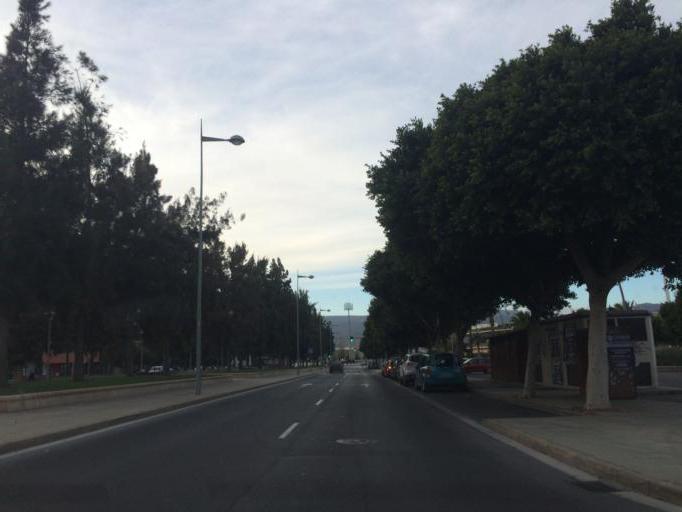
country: ES
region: Andalusia
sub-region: Provincia de Almeria
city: Almeria
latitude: 36.8380
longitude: -2.4330
